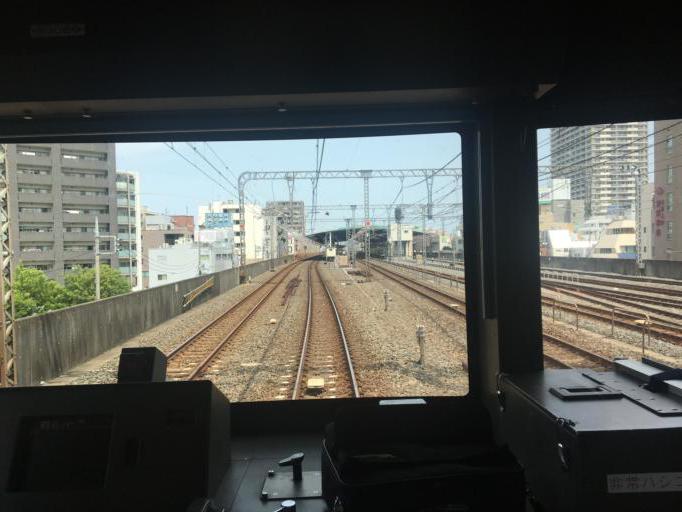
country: JP
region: Saitama
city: Koshigaya
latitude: 35.8860
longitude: 139.7869
